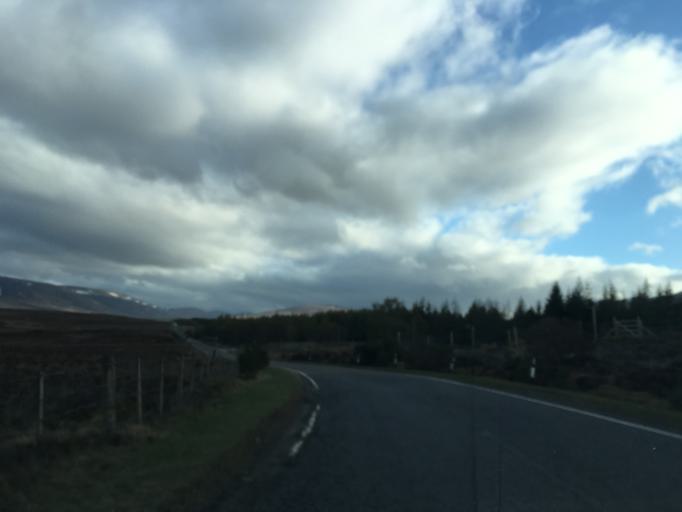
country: GB
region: Scotland
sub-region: Highland
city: Kingussie
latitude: 56.9617
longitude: -4.2445
